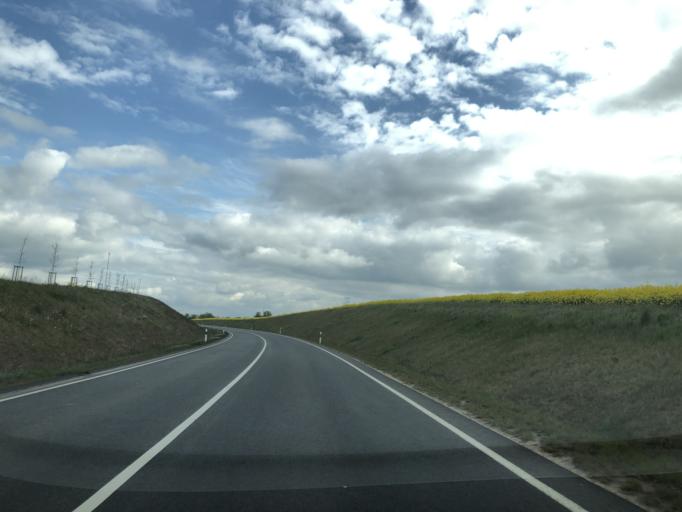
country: DE
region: Mecklenburg-Vorpommern
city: Plau am See
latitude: 53.4628
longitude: 12.2477
